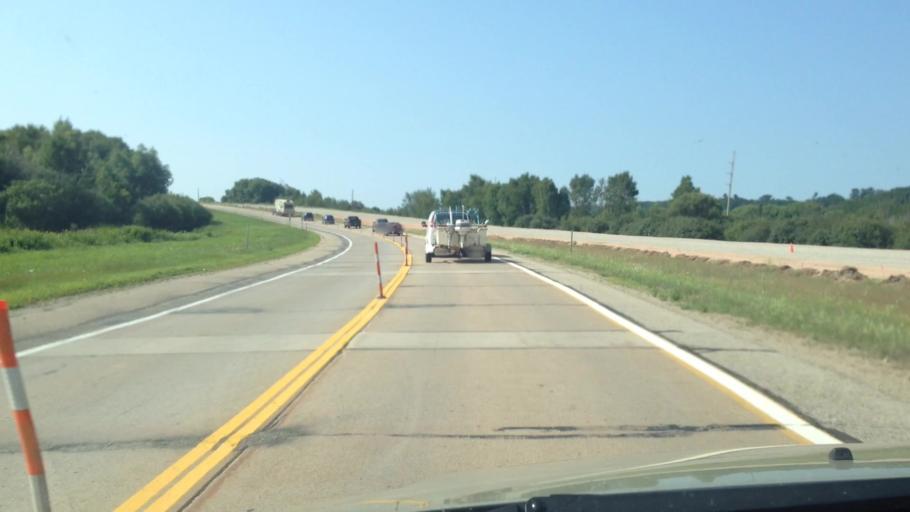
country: US
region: Michigan
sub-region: Delta County
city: Gladstone
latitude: 45.8641
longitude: -87.0264
